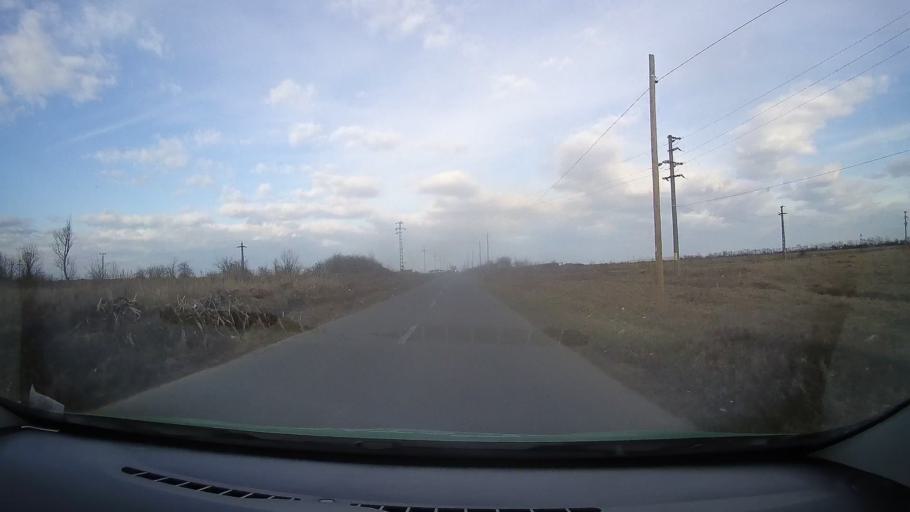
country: RO
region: Dambovita
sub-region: Comuna Vacaresti
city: Vacaresti
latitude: 44.8623
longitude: 25.5124
